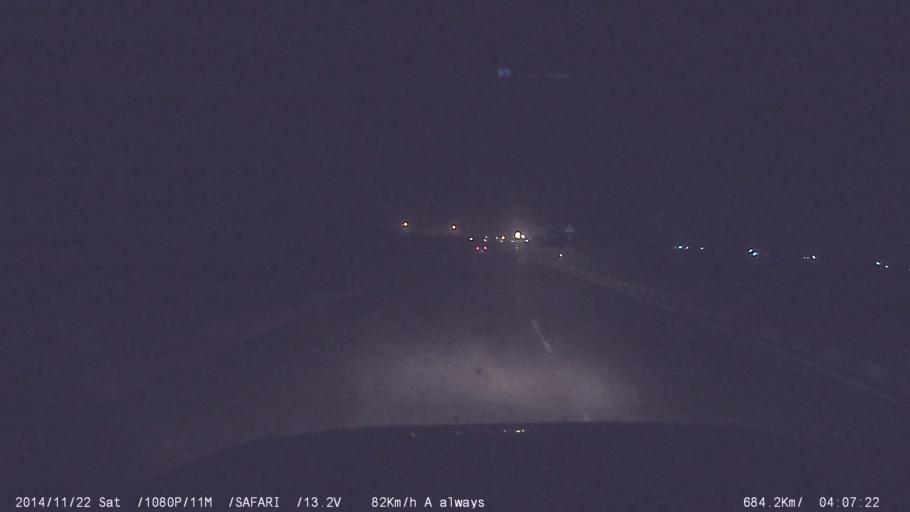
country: IN
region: Tamil Nadu
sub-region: Erode
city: Perundurai
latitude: 11.2888
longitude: 77.5651
